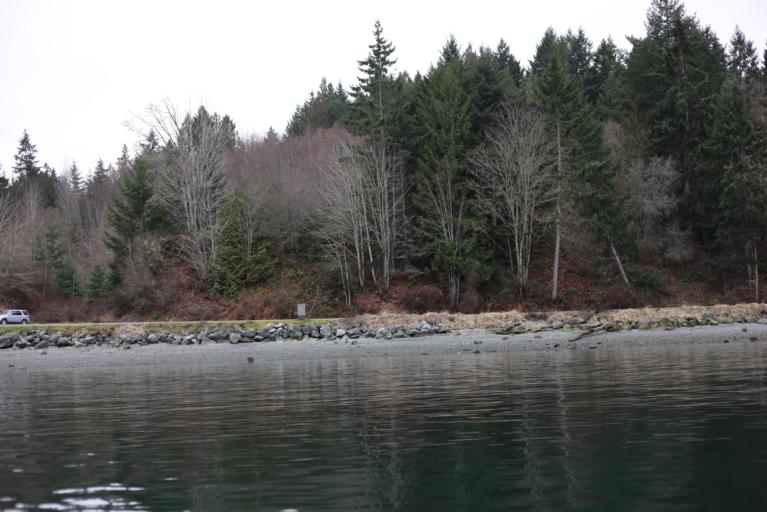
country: CA
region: British Columbia
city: North Saanich
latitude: 48.6345
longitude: -123.5318
